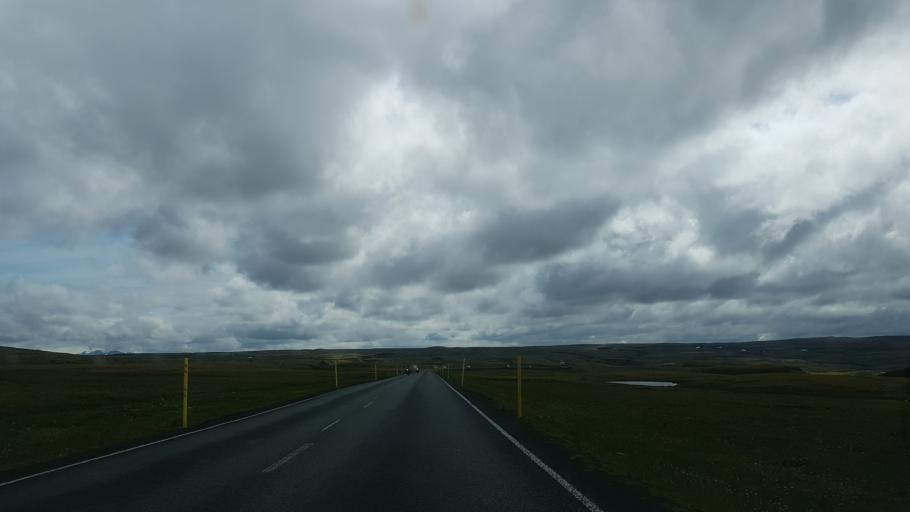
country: IS
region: West
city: Borgarnes
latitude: 64.9538
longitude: -21.0580
